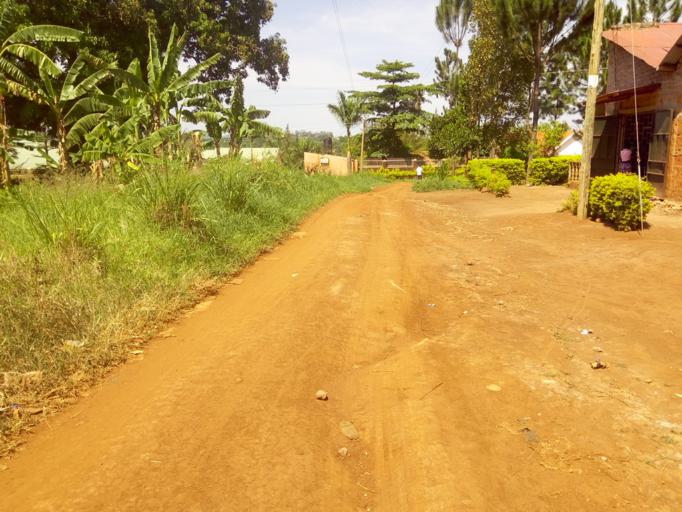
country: UG
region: Western Region
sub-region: Masindi District
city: Masindi
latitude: 1.6893
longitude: 31.7146
